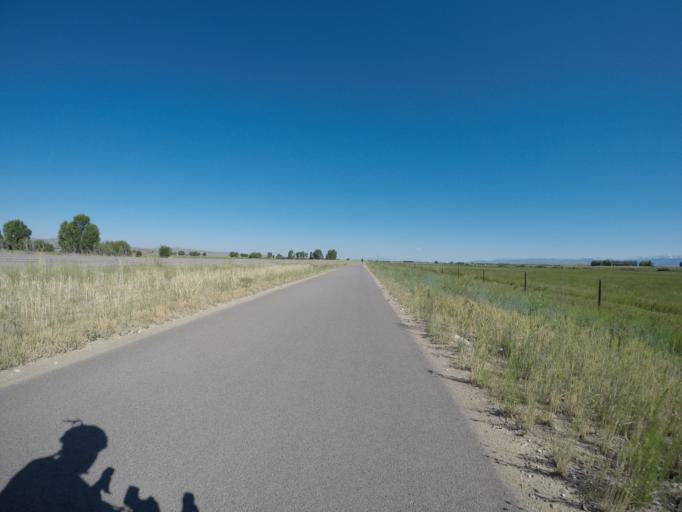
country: US
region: Wyoming
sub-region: Sublette County
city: Pinedale
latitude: 42.8203
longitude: -109.8403
